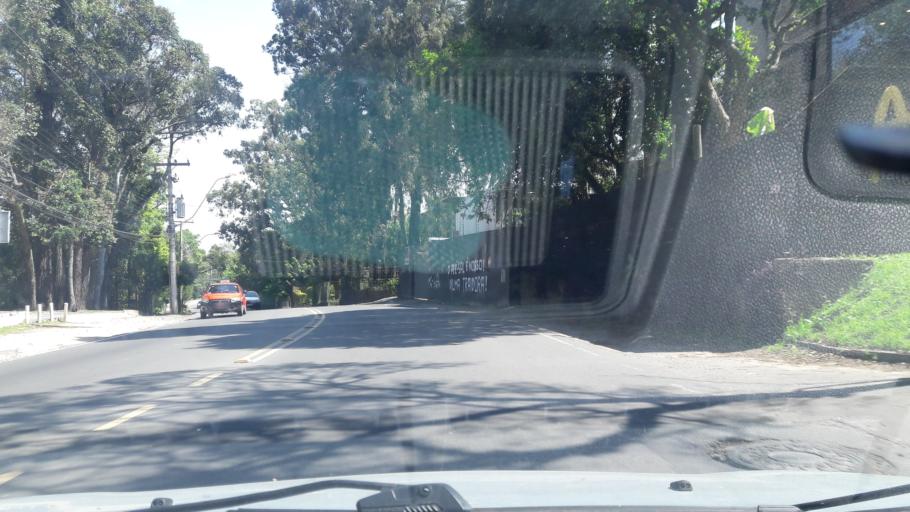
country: BR
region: Rio Grande do Sul
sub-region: Guaiba
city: Guaiba
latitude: -30.1229
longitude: -51.2498
